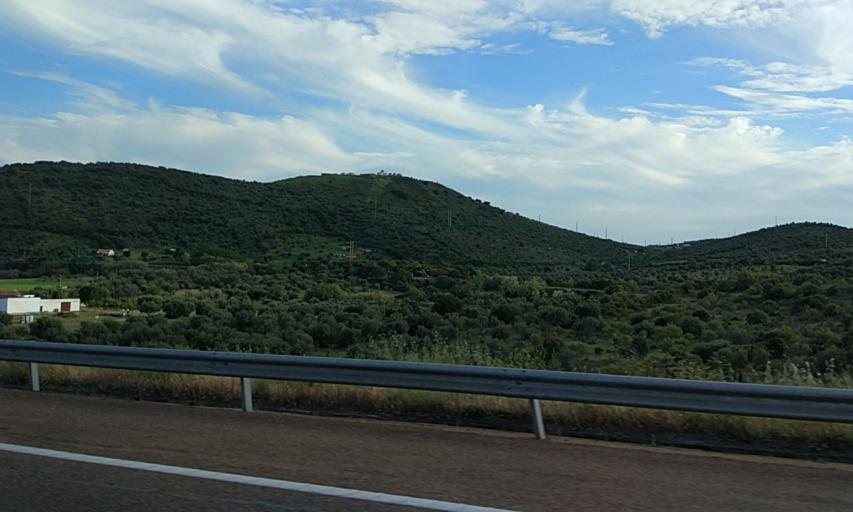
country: PT
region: Portalegre
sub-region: Elvas
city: Elvas
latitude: 38.9078
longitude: -7.1657
